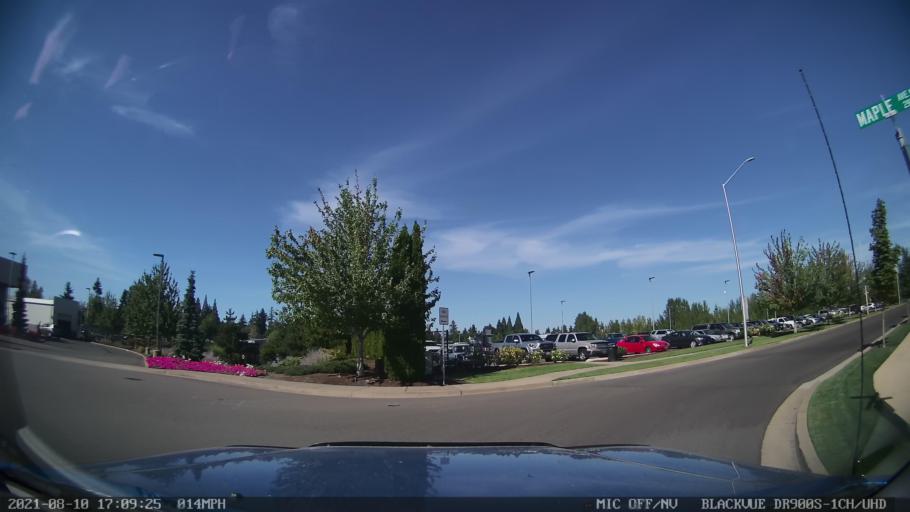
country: US
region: Oregon
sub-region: Marion County
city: Keizer
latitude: 44.9697
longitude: -123.0243
